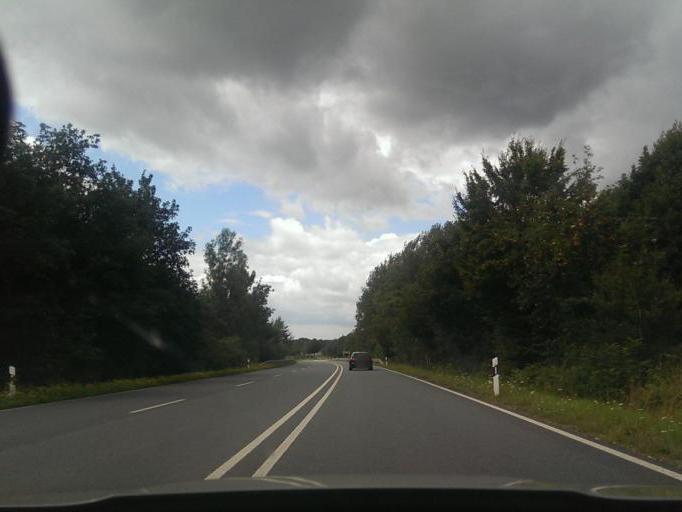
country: DE
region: North Rhine-Westphalia
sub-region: Regierungsbezirk Detmold
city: Schieder-Schwalenberg
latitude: 51.8375
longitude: 9.2574
